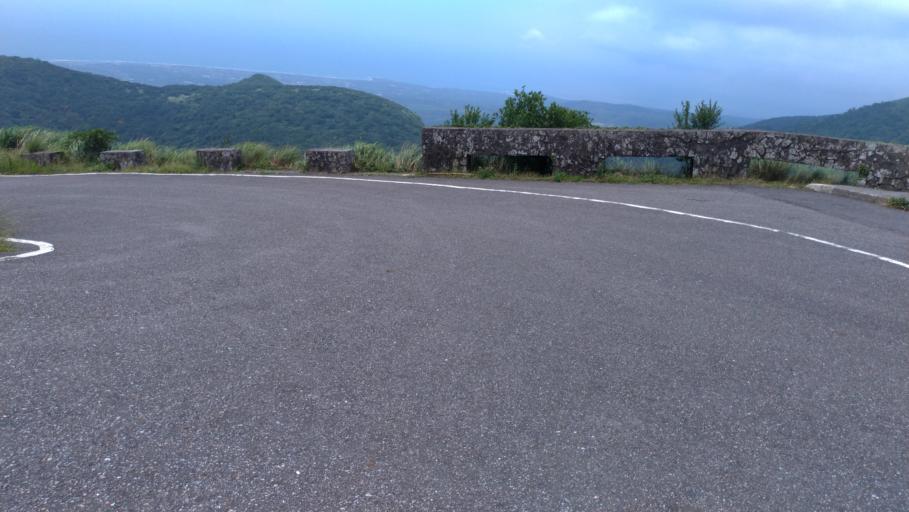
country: TW
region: Taipei
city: Taipei
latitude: 25.1815
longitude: 121.5240
